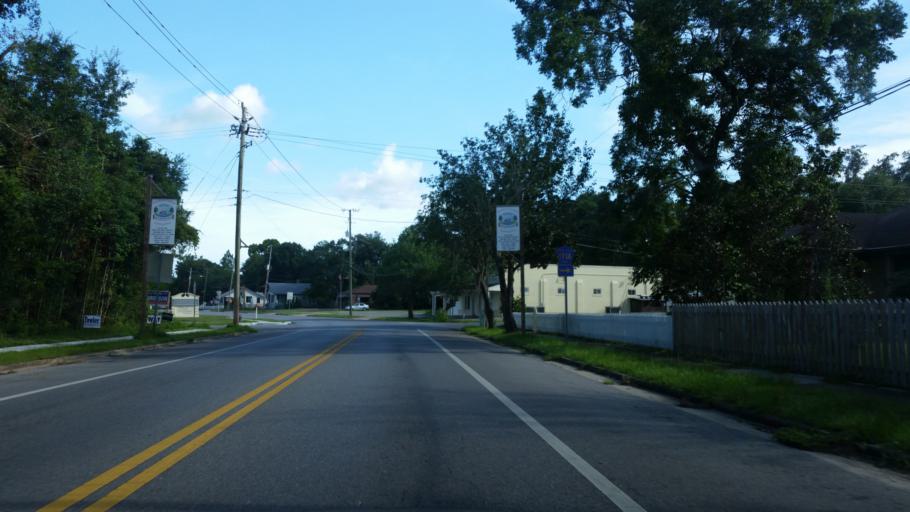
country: US
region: Florida
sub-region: Santa Rosa County
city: Bagdad
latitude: 30.6047
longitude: -87.0344
